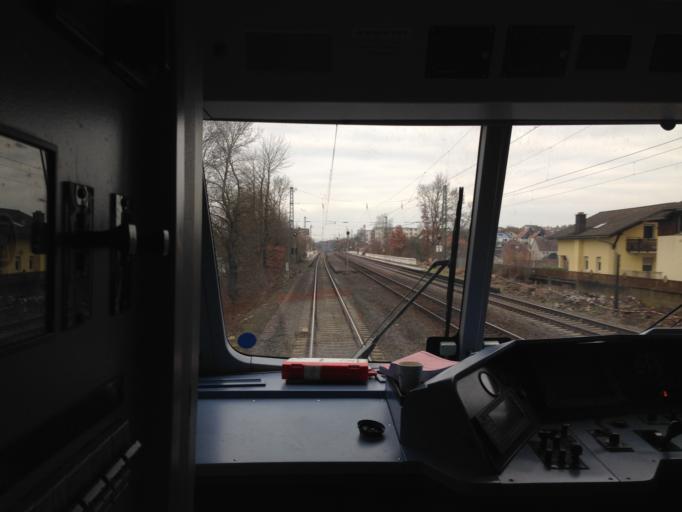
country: DE
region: Hesse
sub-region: Regierungsbezirk Giessen
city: Langgons
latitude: 50.4950
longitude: 8.6669
